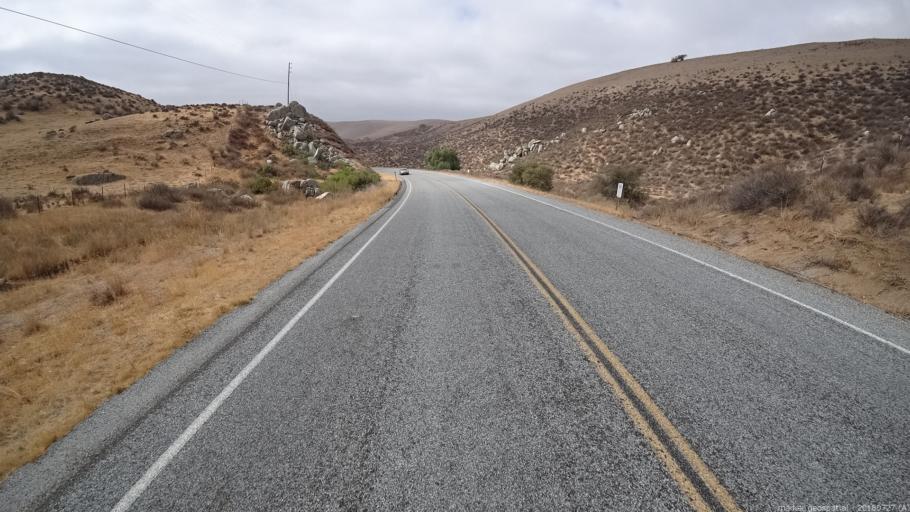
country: US
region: California
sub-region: Monterey County
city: King City
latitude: 36.2767
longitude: -121.0642
